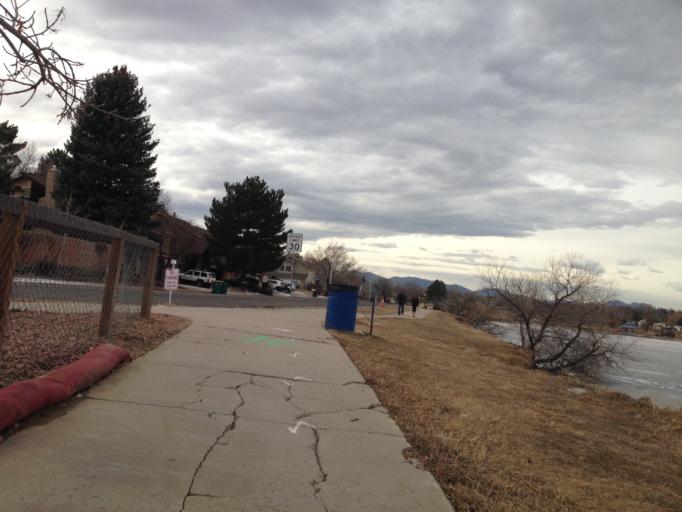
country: US
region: Colorado
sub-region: Adams County
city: Westminster
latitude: 39.8422
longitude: -105.0669
